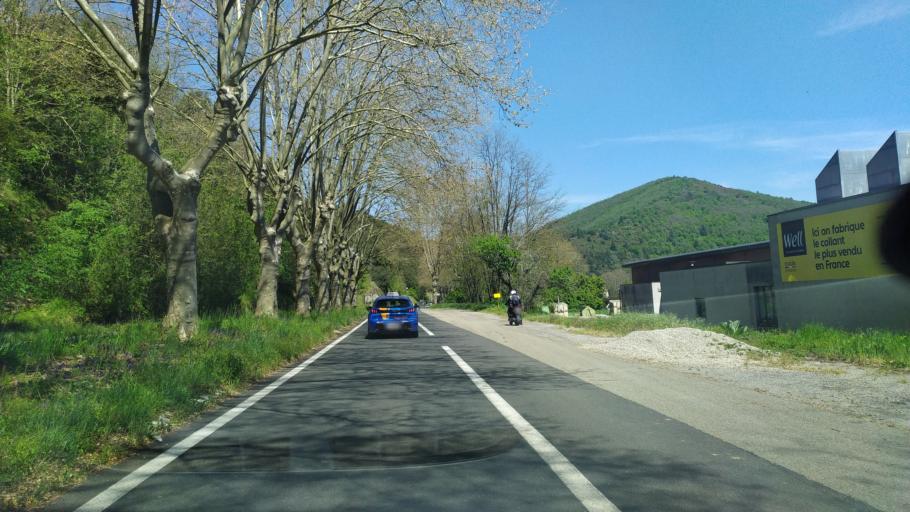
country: FR
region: Languedoc-Roussillon
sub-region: Departement du Gard
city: Le Vigan
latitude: 43.9924
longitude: 3.6289
